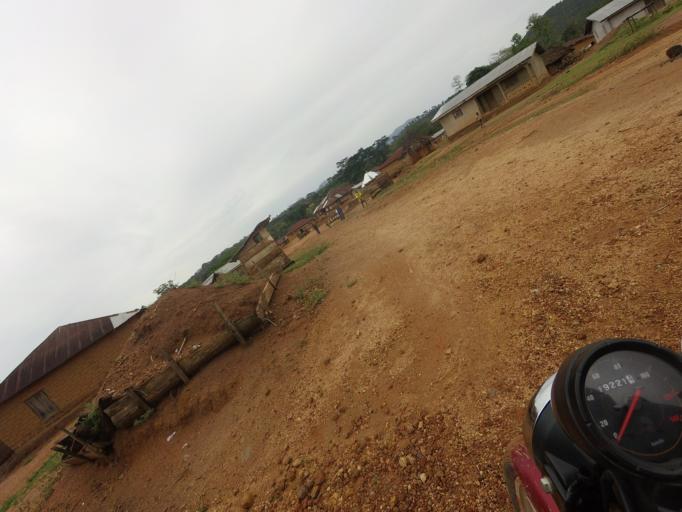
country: LR
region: Nimba
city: New Yekepa
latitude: 7.6527
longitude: -8.5583
